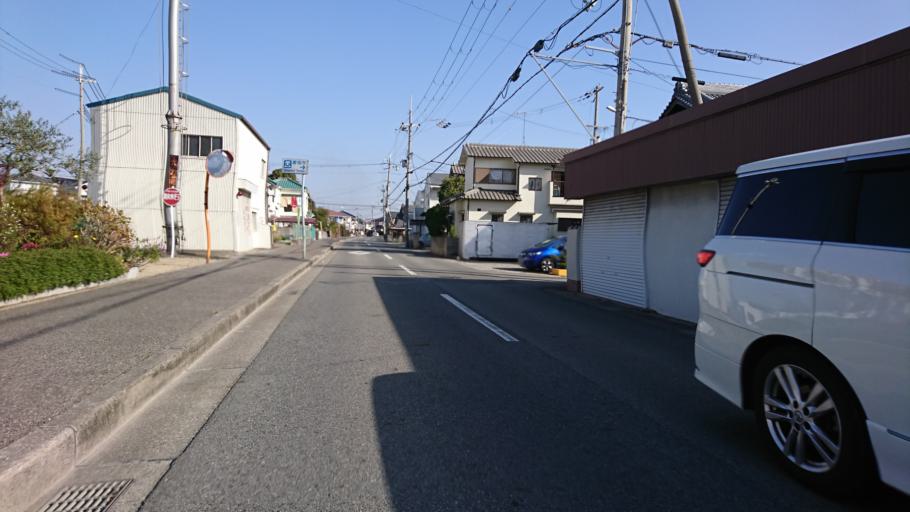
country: JP
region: Hyogo
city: Kakogawacho-honmachi
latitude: 34.7228
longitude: 134.8716
